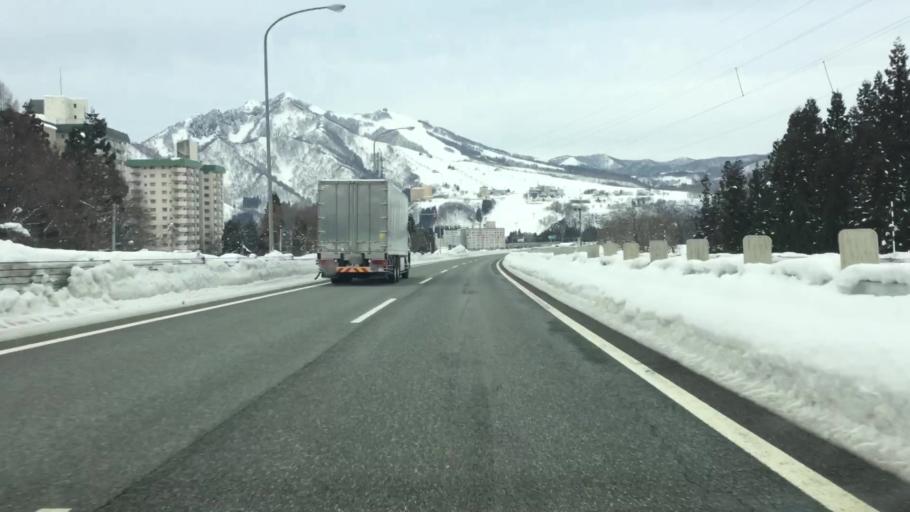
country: JP
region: Niigata
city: Shiozawa
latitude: 36.9151
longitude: 138.8396
